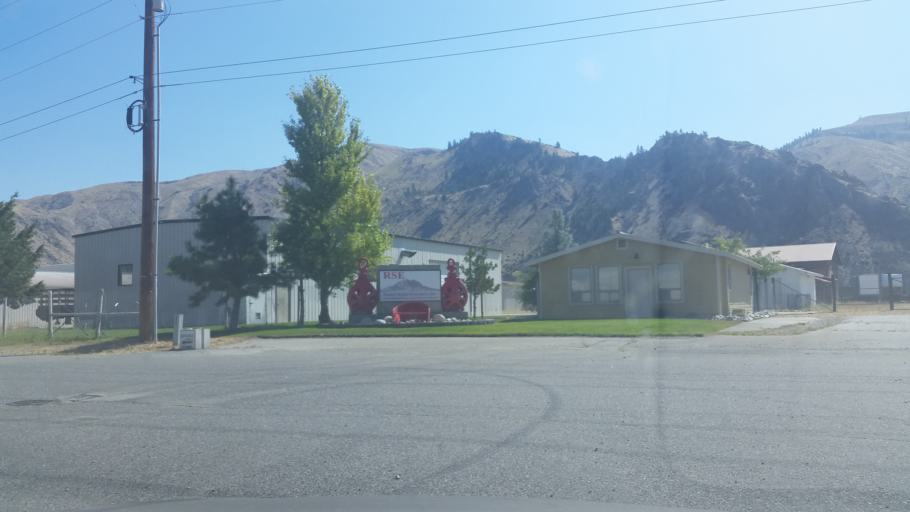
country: US
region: Washington
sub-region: Chelan County
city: Entiat
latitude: 47.6818
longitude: -120.2062
